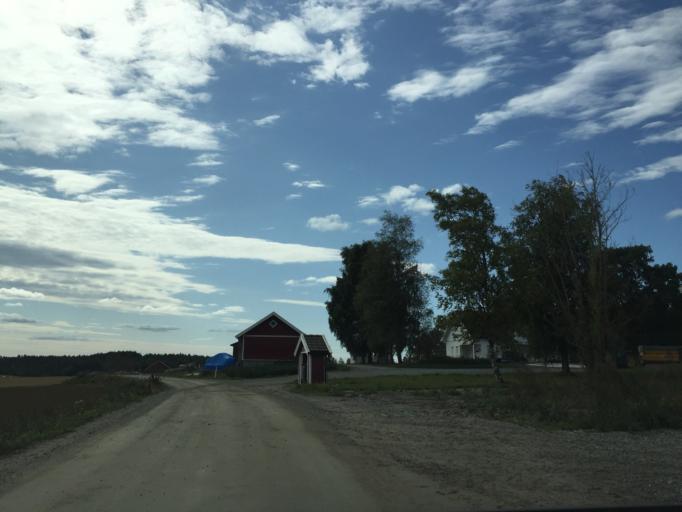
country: NO
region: Ostfold
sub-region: Hobol
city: Elvestad
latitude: 59.6379
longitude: 10.8876
